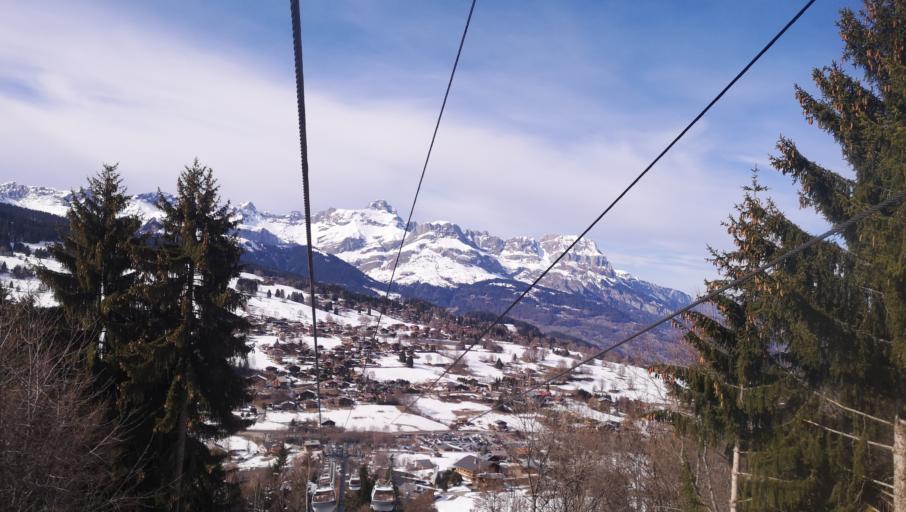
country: FR
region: Rhone-Alpes
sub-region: Departement de la Haute-Savoie
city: Combloux
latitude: 45.8757
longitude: 6.6466
